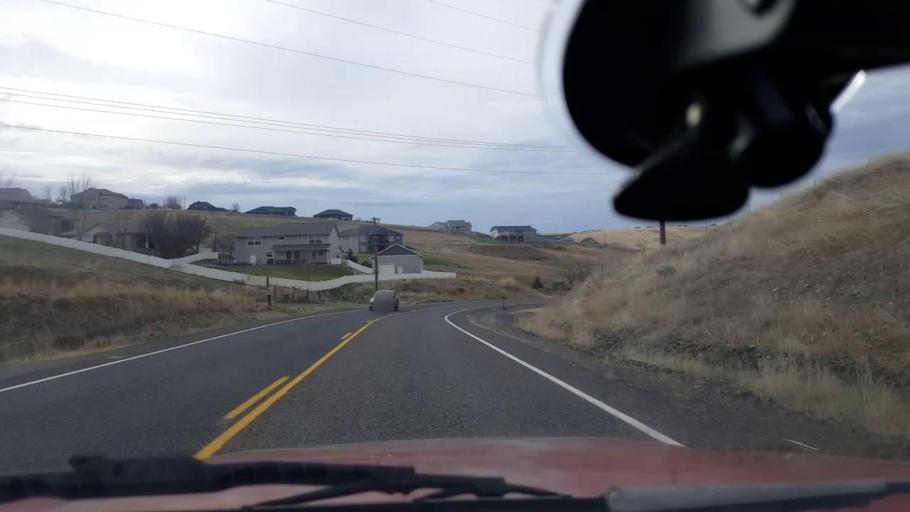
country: US
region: Washington
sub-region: Asotin County
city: Clarkston Heights-Vineland
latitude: 46.3999
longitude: -117.0917
